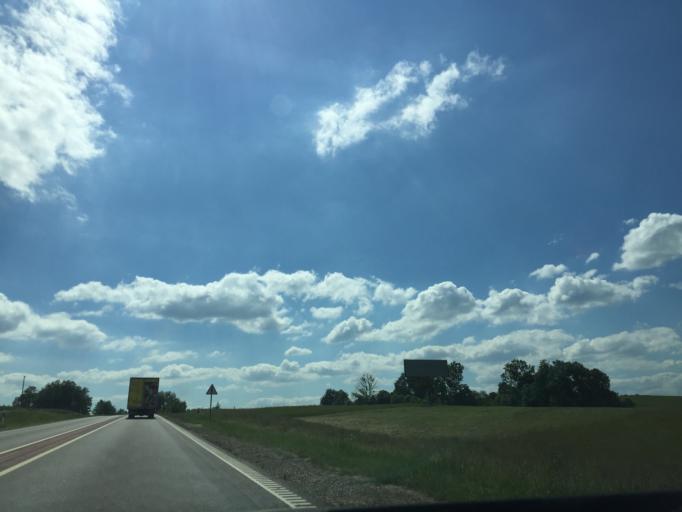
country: LT
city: Kalvarija
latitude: 54.3519
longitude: 23.1747
